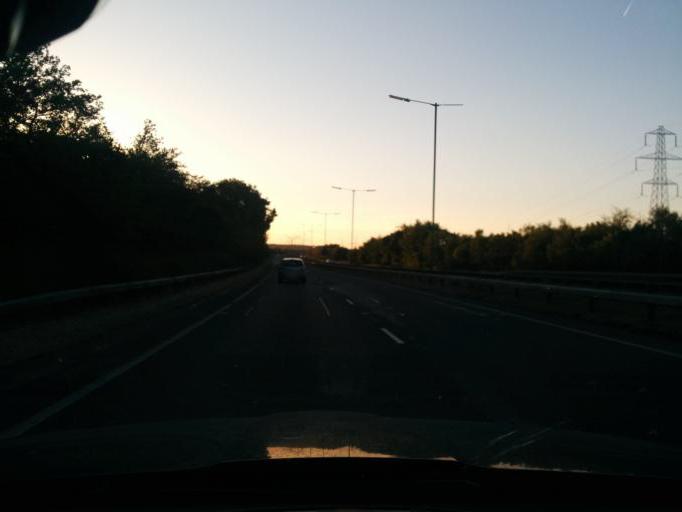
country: GB
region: England
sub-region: Northumberland
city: Newbiggin-by-the-Sea
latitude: 55.1797
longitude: -1.5331
